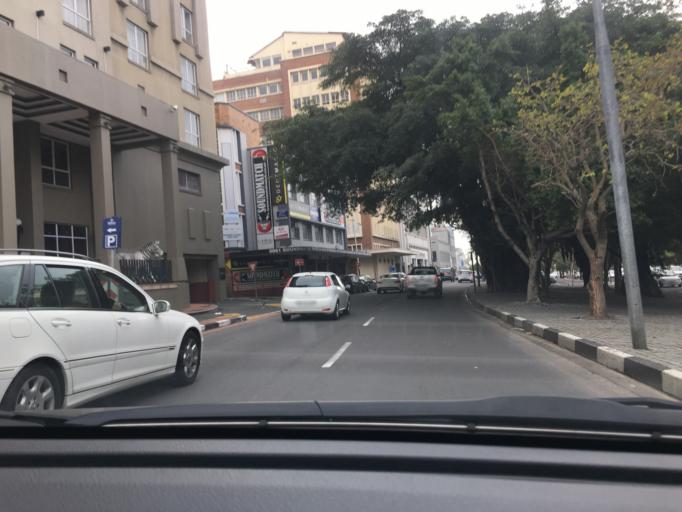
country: ZA
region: Western Cape
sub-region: City of Cape Town
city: Cape Town
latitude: -33.9218
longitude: 18.4160
